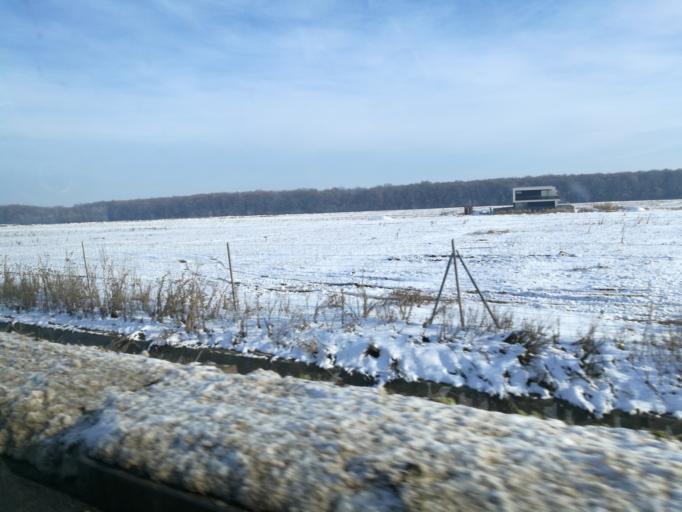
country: RO
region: Ilfov
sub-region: Voluntari City
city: Voluntari
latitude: 44.5058
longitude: 26.1597
